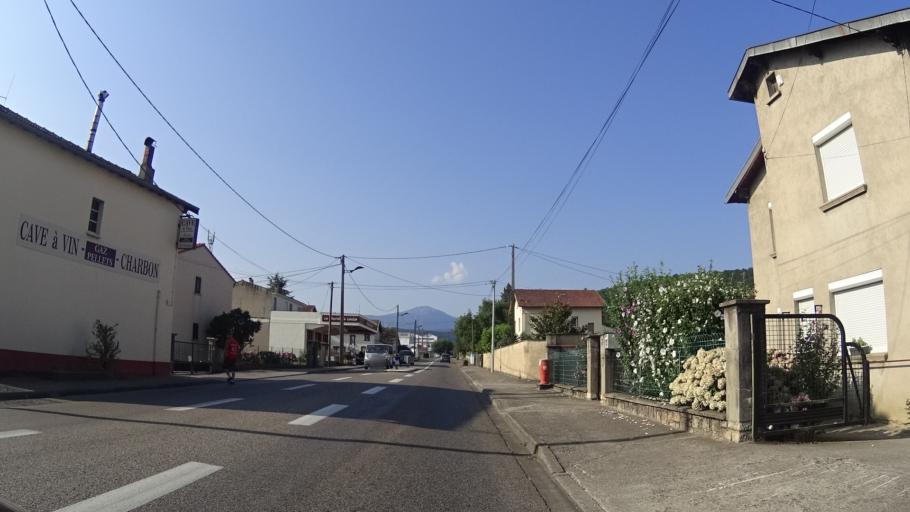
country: FR
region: Midi-Pyrenees
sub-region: Departement de l'Ariege
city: Lavelanet
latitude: 42.9659
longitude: 1.8652
